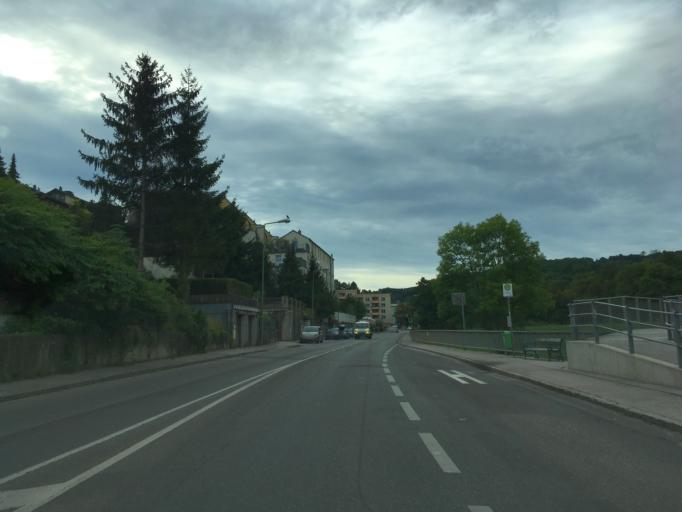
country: AT
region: Lower Austria
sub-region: Politischer Bezirk Wien-Umgebung
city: Klosterneuburg
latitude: 48.3067
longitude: 16.2880
